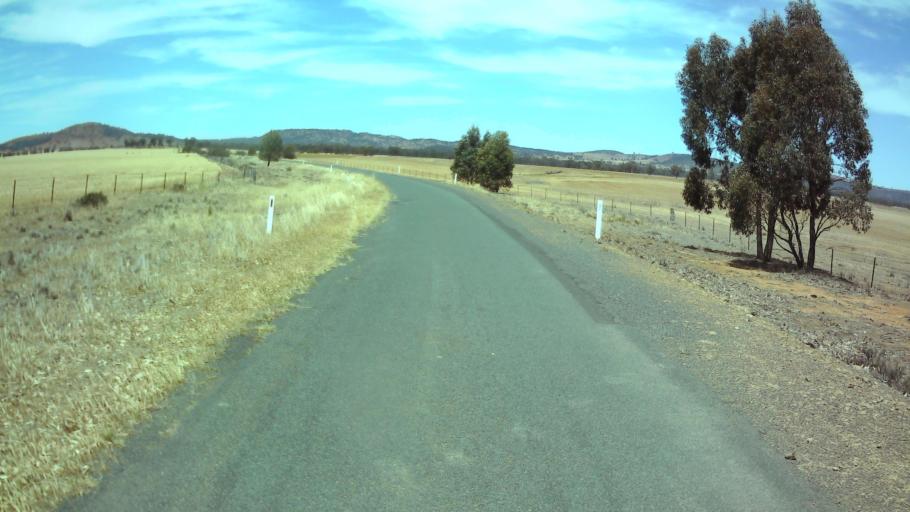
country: AU
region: New South Wales
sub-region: Weddin
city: Grenfell
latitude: -33.7589
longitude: 148.1016
